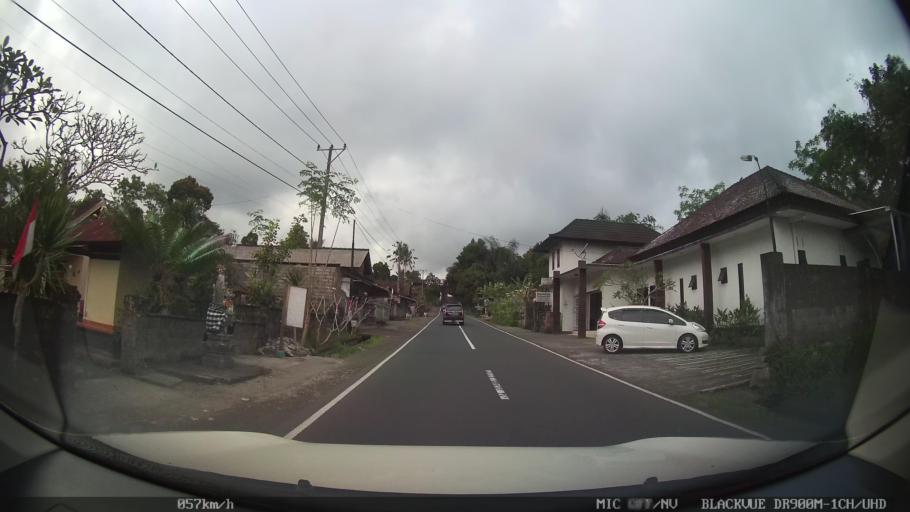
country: ID
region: Bali
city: Banjar Tiga
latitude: -8.3785
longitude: 115.4180
